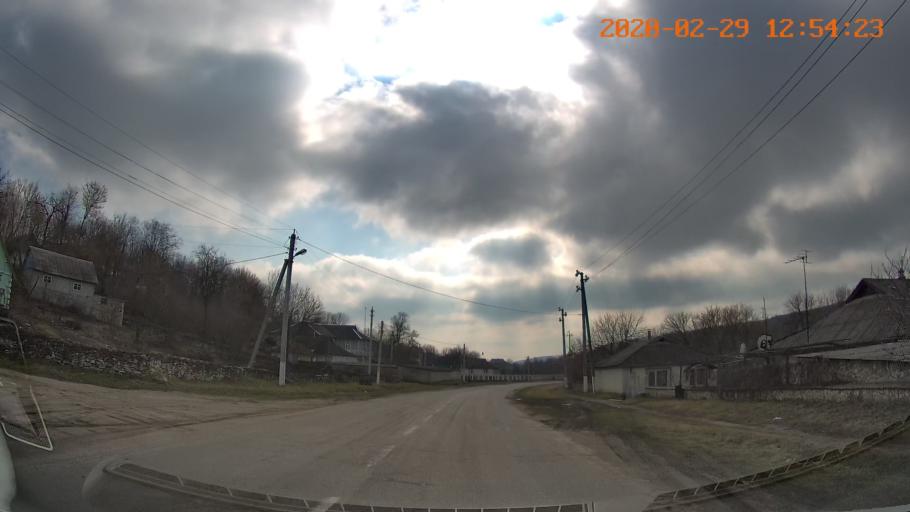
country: MD
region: Telenesti
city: Camenca
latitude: 48.1022
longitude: 28.7277
